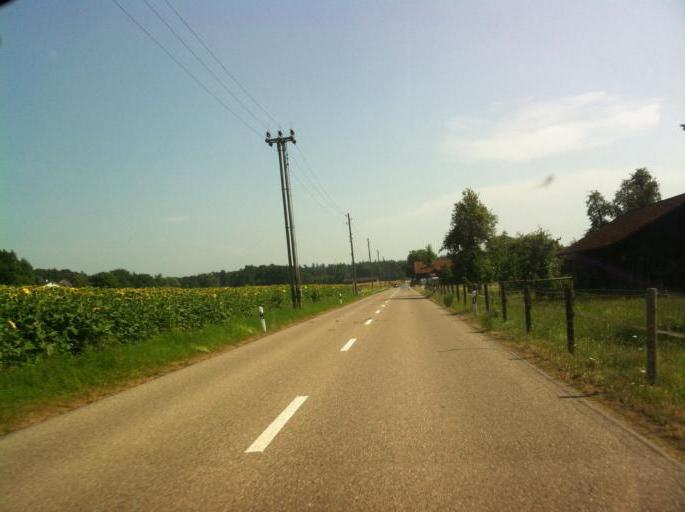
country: CH
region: Zurich
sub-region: Bezirk Andelfingen
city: Kleinandelfingen
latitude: 47.6321
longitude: 8.6919
